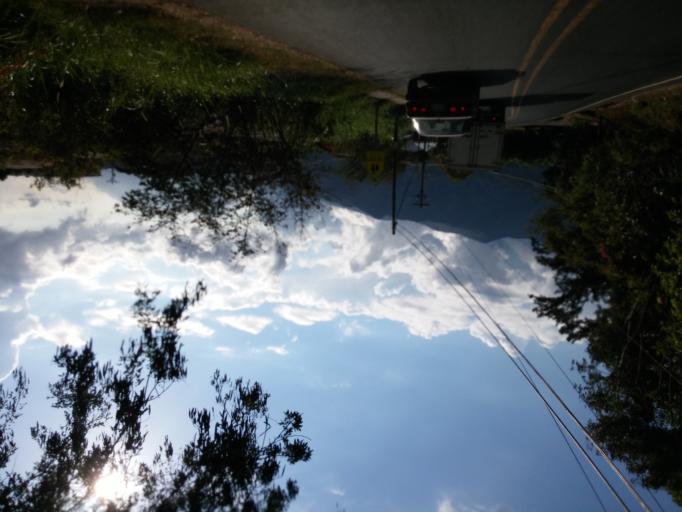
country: CR
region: San Jose
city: San Ignacio
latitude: 9.7959
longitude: -84.1452
